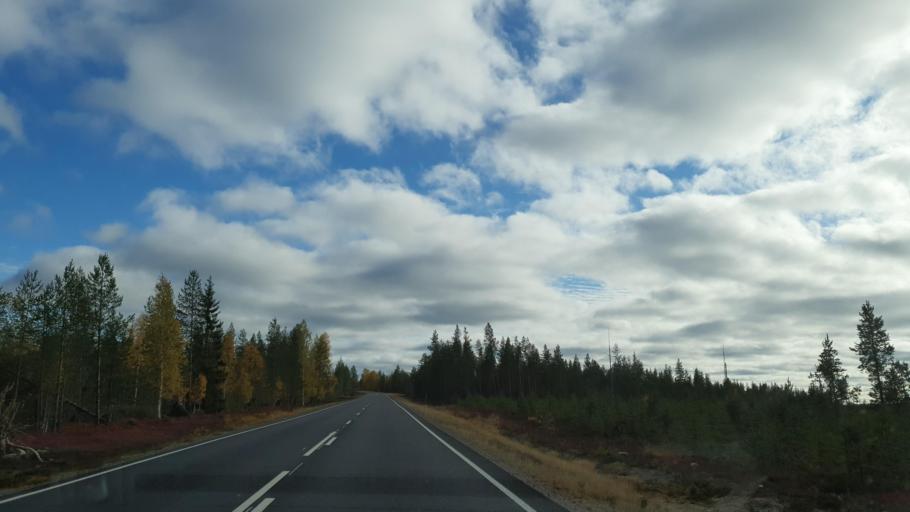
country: FI
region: Northern Ostrobothnia
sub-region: Oulunkaari
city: Pudasjaervi
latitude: 65.3436
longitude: 27.4049
